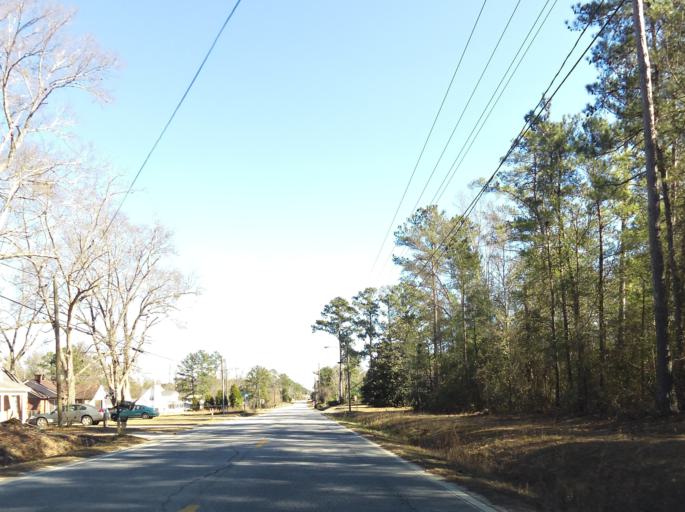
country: US
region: Georgia
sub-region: Bibb County
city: West Point
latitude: 32.8050
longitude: -83.7971
